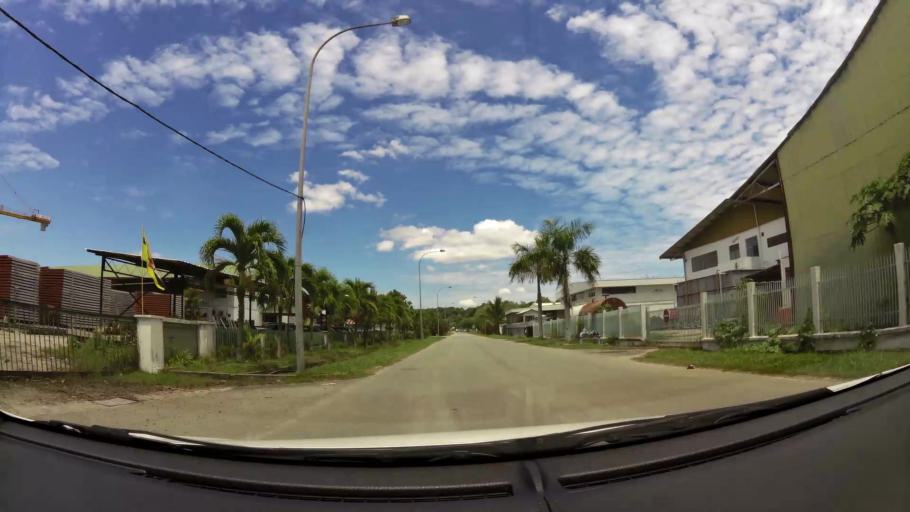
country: BN
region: Brunei and Muara
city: Bandar Seri Begawan
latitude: 4.9975
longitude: 115.0282
